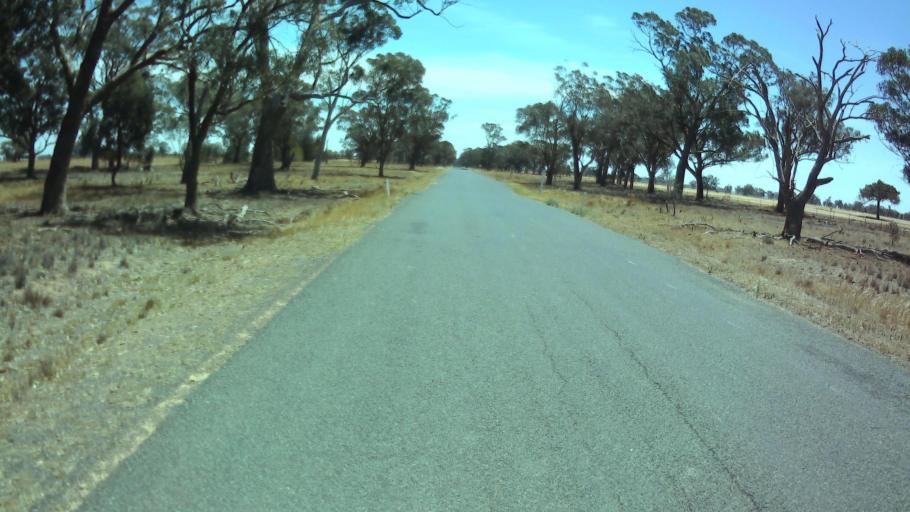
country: AU
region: New South Wales
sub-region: Weddin
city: Grenfell
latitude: -34.0056
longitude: 147.7718
